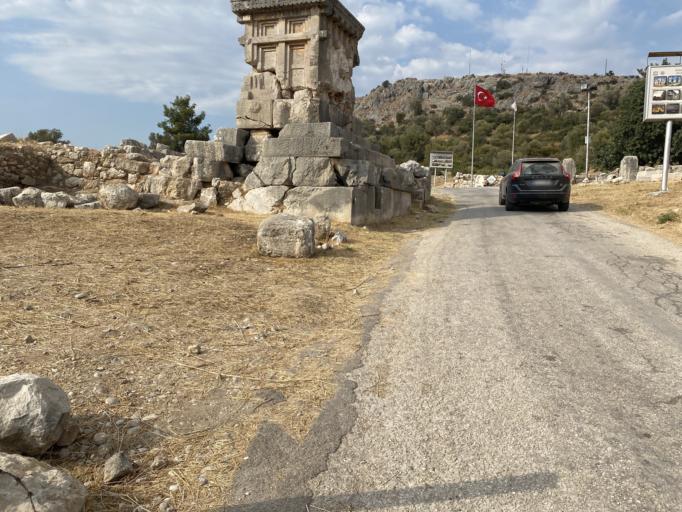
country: TR
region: Mugla
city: Esen
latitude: 36.3568
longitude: 29.3187
